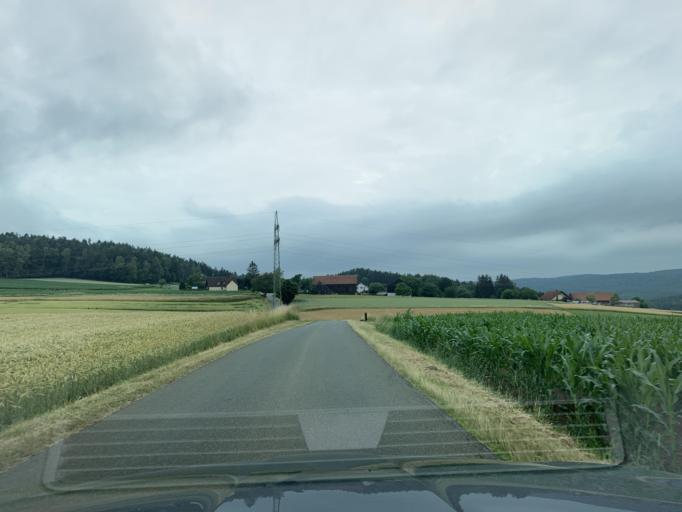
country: DE
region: Bavaria
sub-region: Upper Palatinate
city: Winklarn
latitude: 49.4252
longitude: 12.4630
